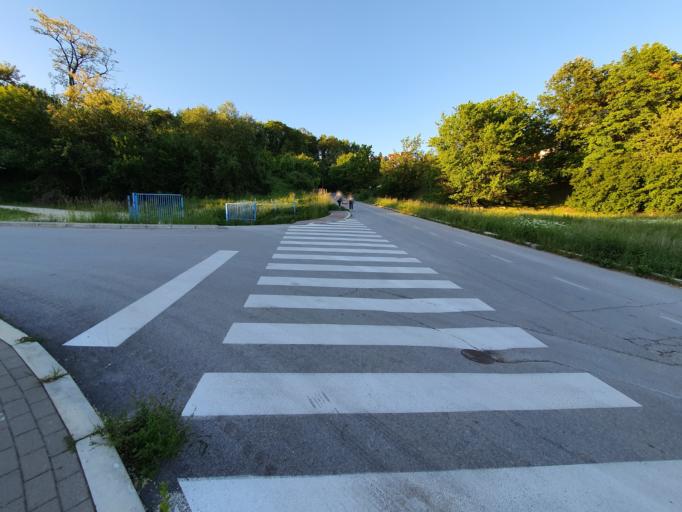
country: RS
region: Central Serbia
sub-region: Zlatiborski Okrug
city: Uzice
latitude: 43.8545
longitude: 19.8582
